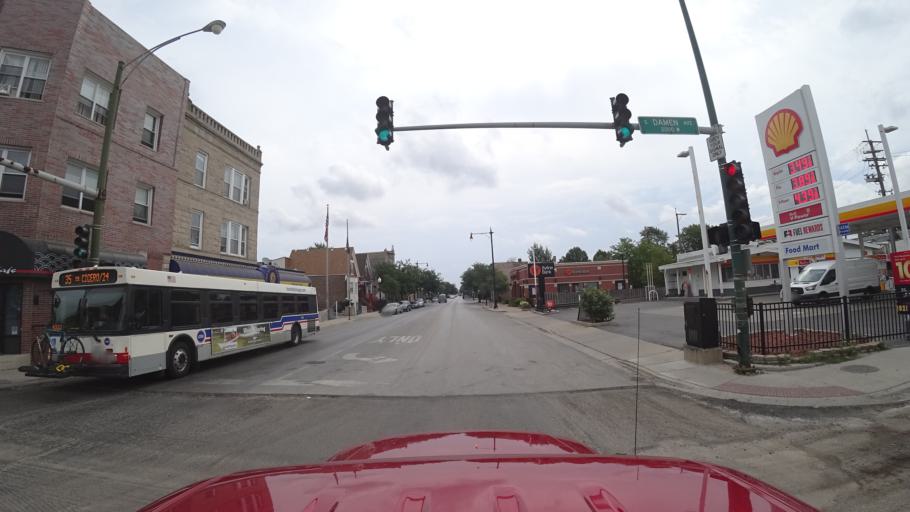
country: US
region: Illinois
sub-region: Cook County
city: Chicago
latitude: 41.8304
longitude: -87.6753
